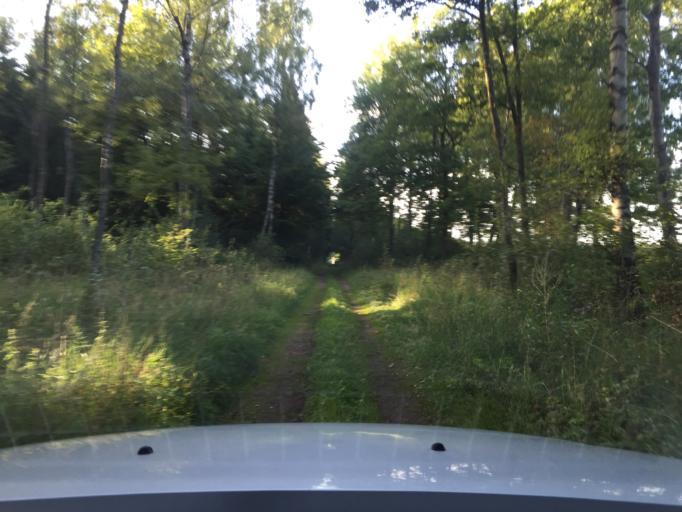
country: SE
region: Skane
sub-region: Hassleholms Kommun
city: Sosdala
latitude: 56.0188
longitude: 13.7145
